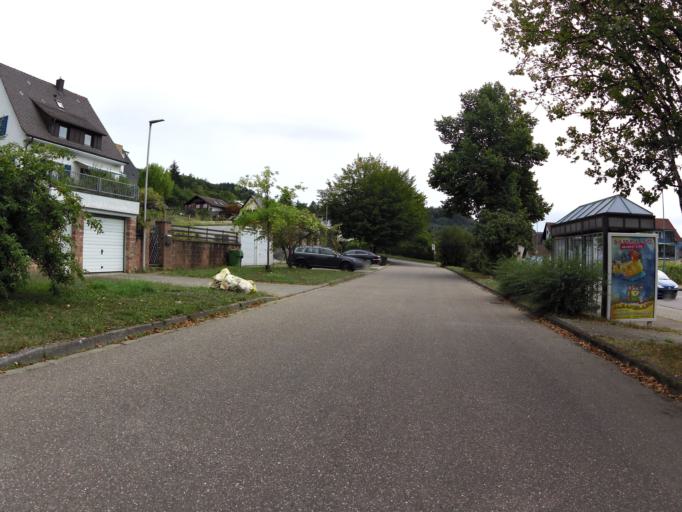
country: DE
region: Baden-Wuerttemberg
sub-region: Freiburg Region
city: Hohberg
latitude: 48.3405
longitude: 7.8999
